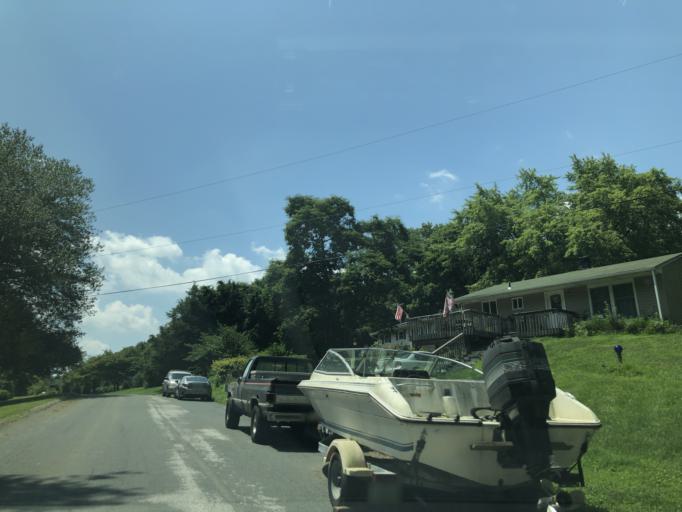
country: US
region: Maryland
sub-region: Carroll County
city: Westminster
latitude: 39.5283
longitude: -76.9384
